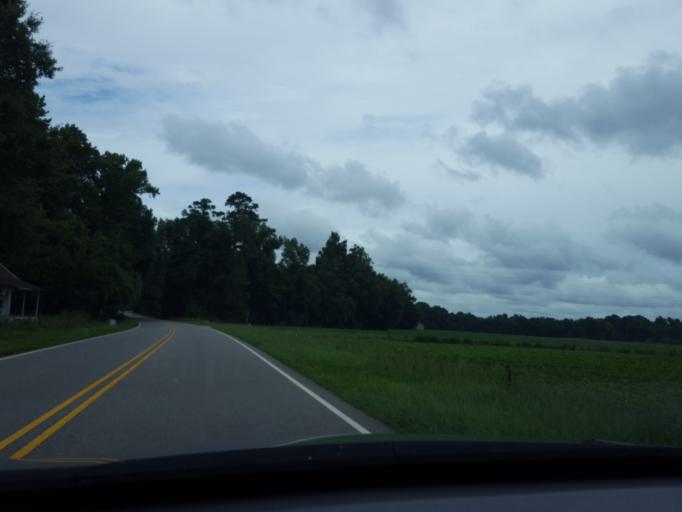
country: US
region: North Carolina
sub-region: Beaufort County
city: Washington
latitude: 35.6911
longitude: -76.9901
